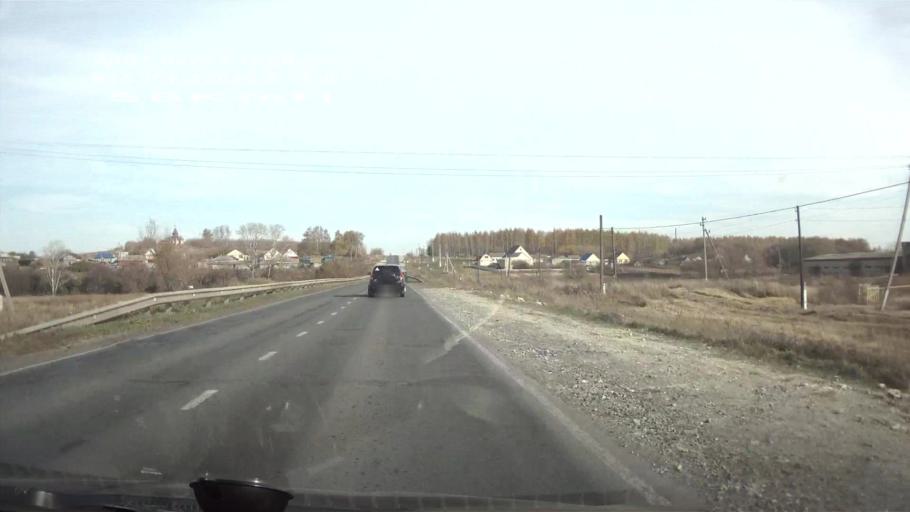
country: RU
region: Mordoviya
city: Atyashevo
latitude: 54.5610
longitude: 45.9776
